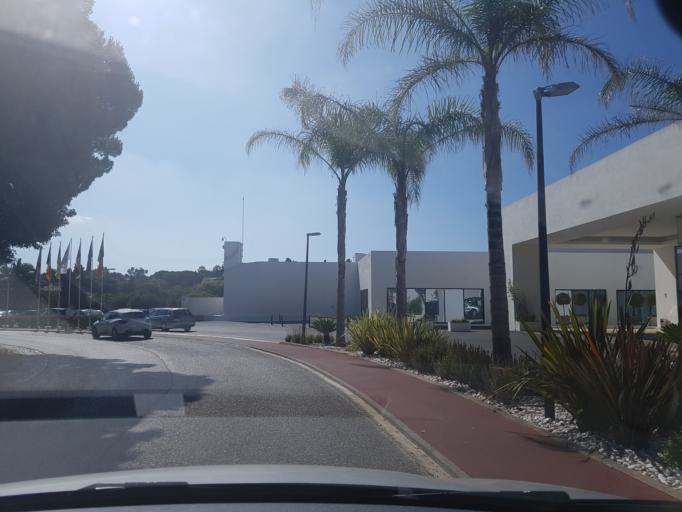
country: PT
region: Faro
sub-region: Lagoa
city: Carvoeiro
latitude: 37.0944
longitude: -8.4599
